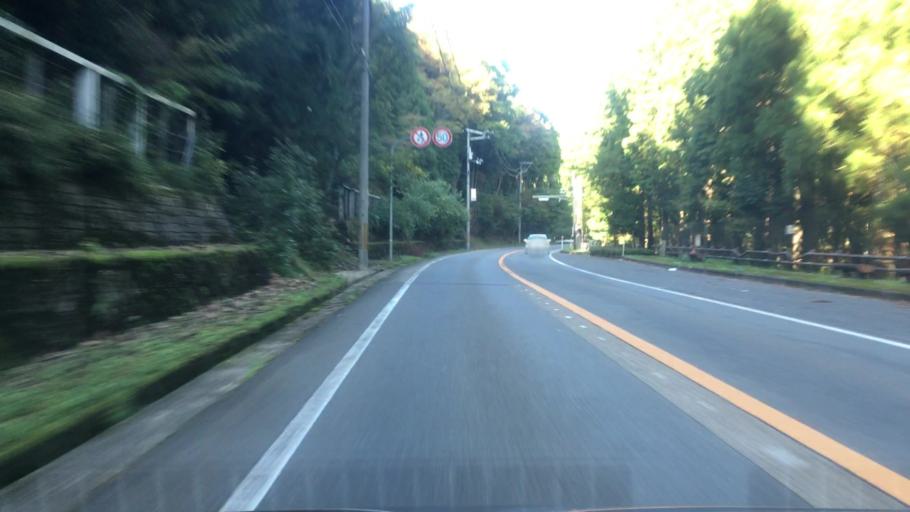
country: JP
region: Hyogo
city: Toyooka
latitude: 35.5802
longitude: 134.8568
